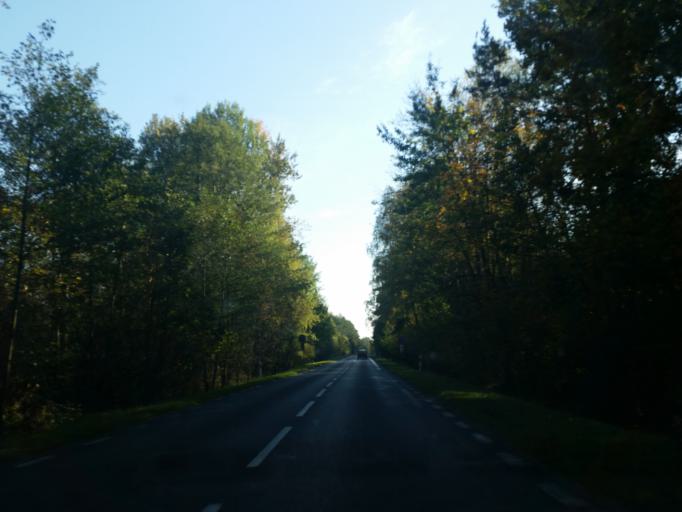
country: PL
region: Masovian Voivodeship
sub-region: Powiat sierpecki
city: Sierpc
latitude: 52.8940
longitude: 19.6506
